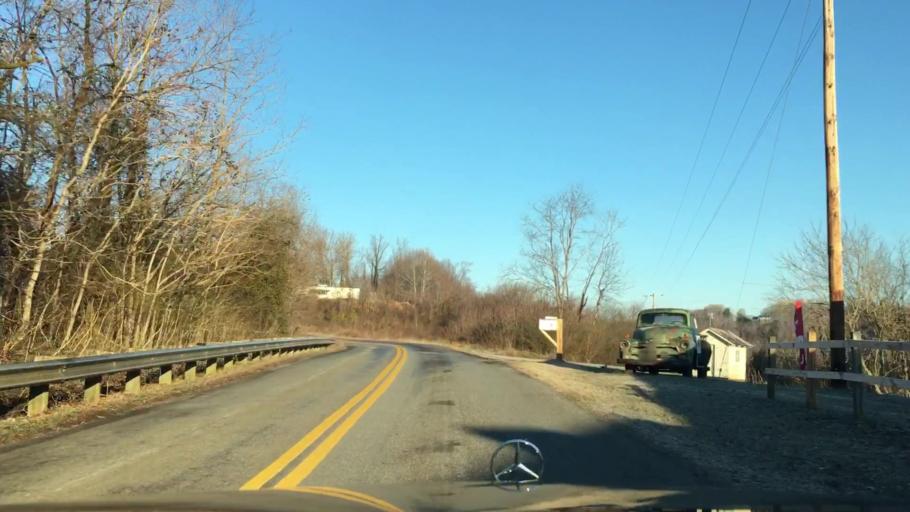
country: US
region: Virginia
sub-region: Pittsylvania County
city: Hurt
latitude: 37.1079
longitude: -79.3072
